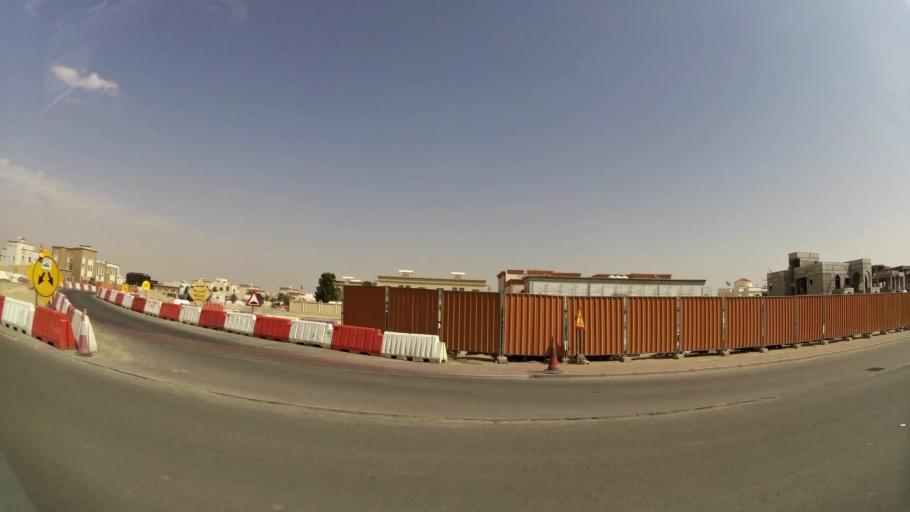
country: AE
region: Abu Dhabi
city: Abu Dhabi
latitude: 24.3172
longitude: 54.5398
